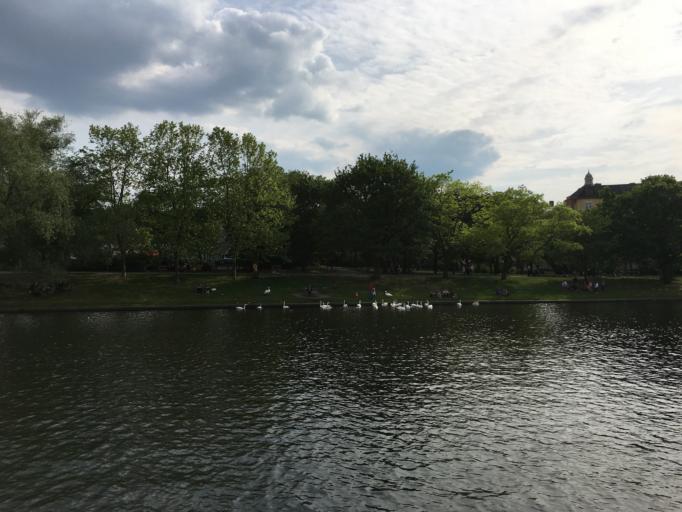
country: DE
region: Berlin
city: Bezirk Kreuzberg
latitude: 52.4960
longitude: 13.4085
